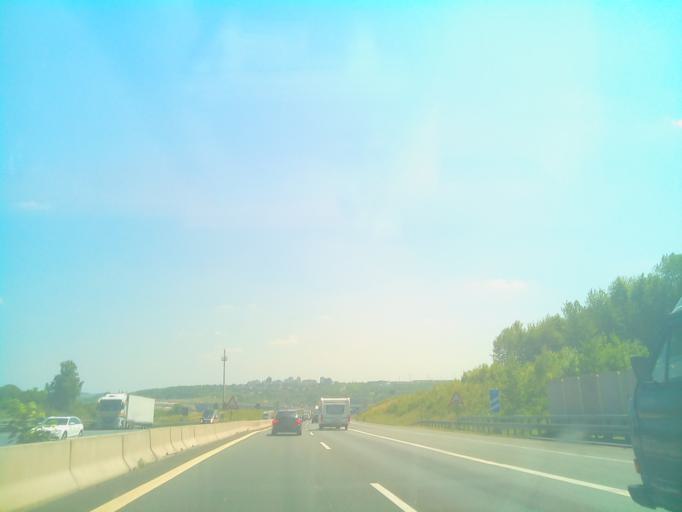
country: DE
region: Bavaria
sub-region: Regierungsbezirk Unterfranken
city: Reichenberg
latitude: 49.7546
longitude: 9.9184
